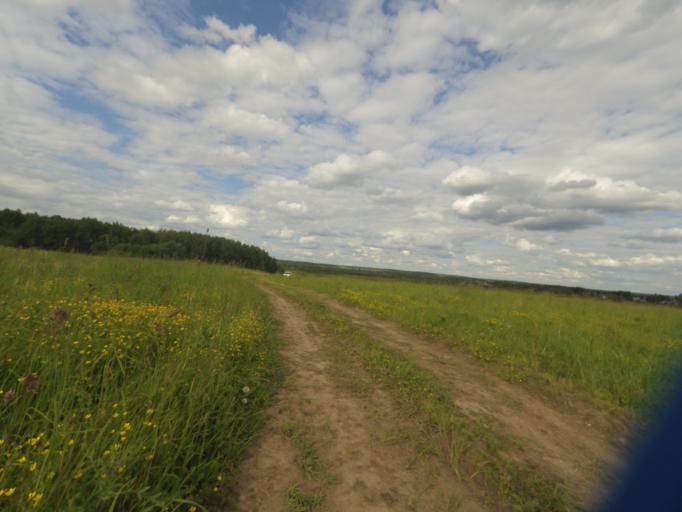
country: RU
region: Moskovskaya
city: Marfino
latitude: 56.1076
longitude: 37.5795
